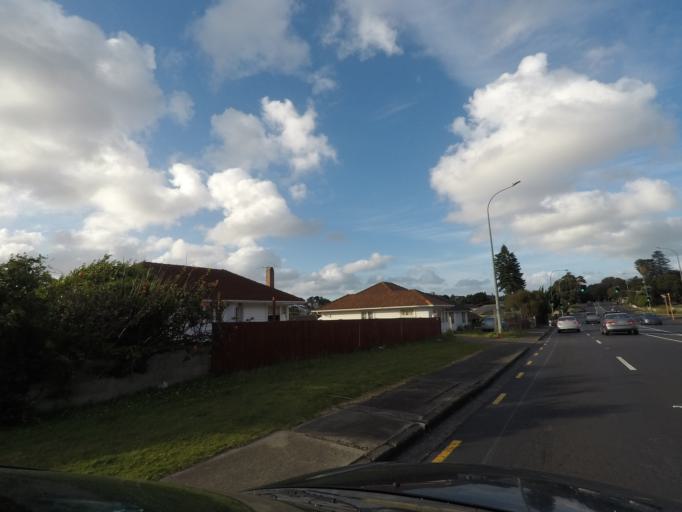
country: NZ
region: Auckland
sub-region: Auckland
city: Auckland
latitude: -36.9161
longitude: 174.7588
